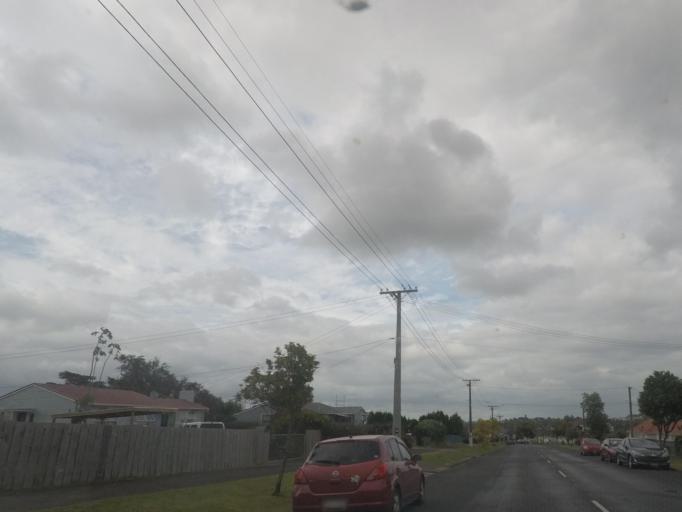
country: NZ
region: Auckland
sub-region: Auckland
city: Tamaki
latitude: -36.8723
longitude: 174.8749
